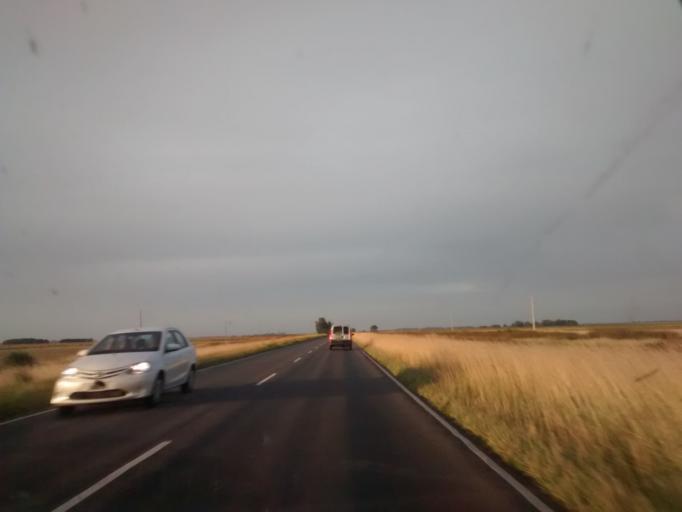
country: AR
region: Buenos Aires
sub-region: Partido de General Belgrano
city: General Belgrano
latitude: -35.9607
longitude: -58.6209
